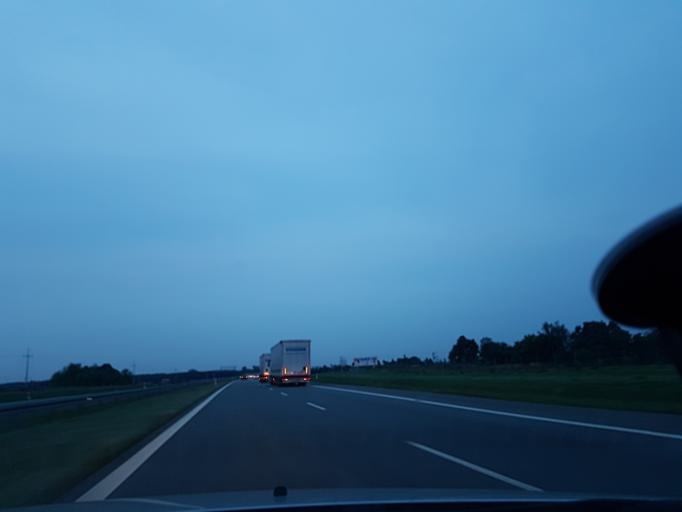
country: PL
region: Lodz Voivodeship
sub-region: Powiat kutnowski
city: Krzyzanow
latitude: 52.2101
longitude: 19.4806
